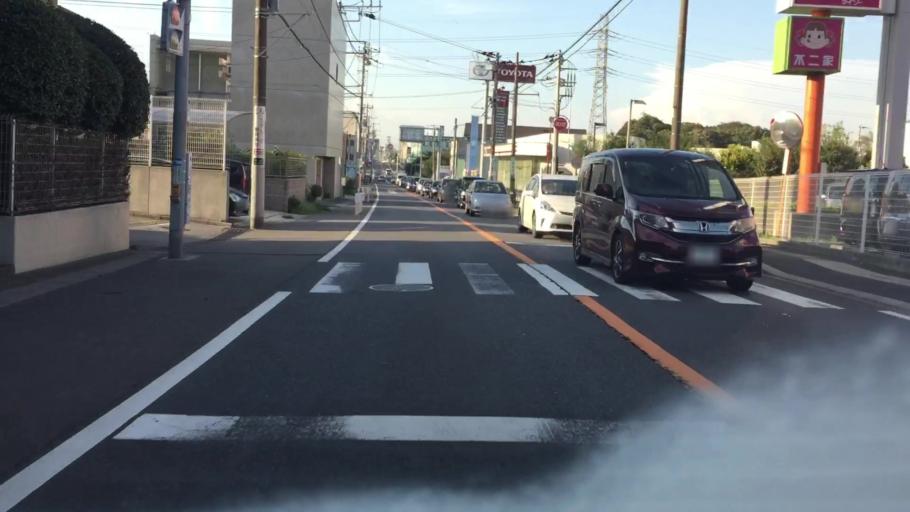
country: JP
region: Chiba
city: Funabashi
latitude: 35.7489
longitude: 139.9988
